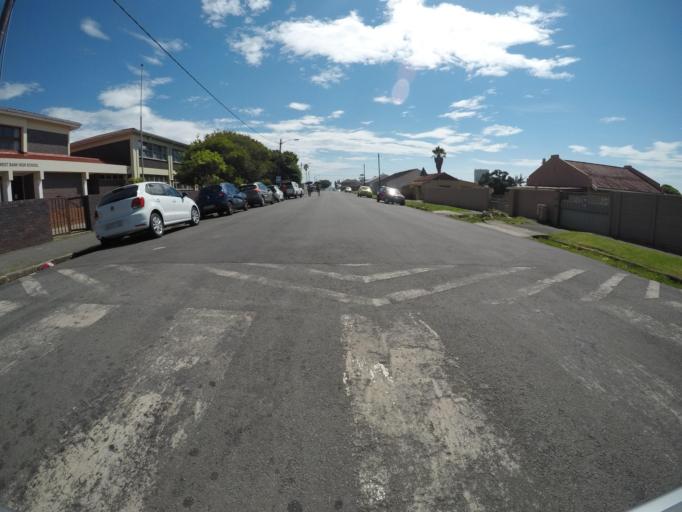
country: ZA
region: Eastern Cape
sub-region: Buffalo City Metropolitan Municipality
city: East London
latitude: -33.0342
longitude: 27.9062
